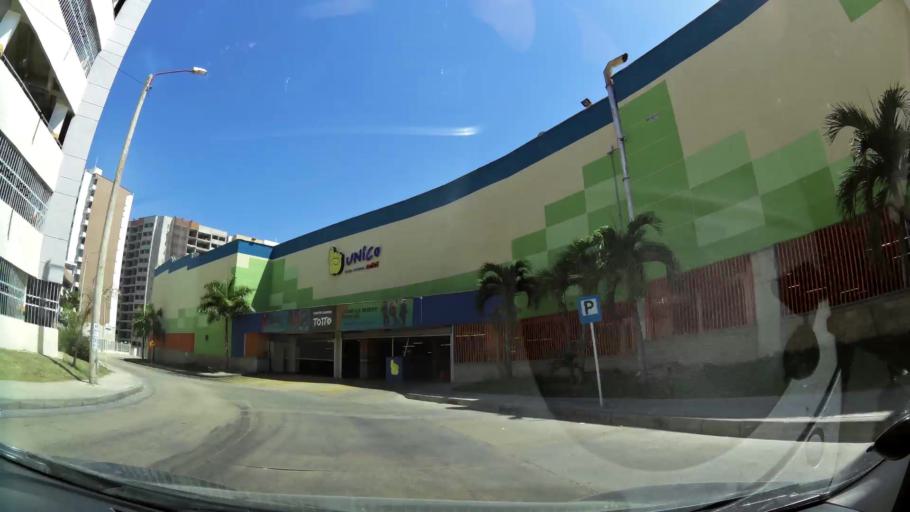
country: CO
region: Atlantico
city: Barranquilla
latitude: 10.9899
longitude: -74.8127
